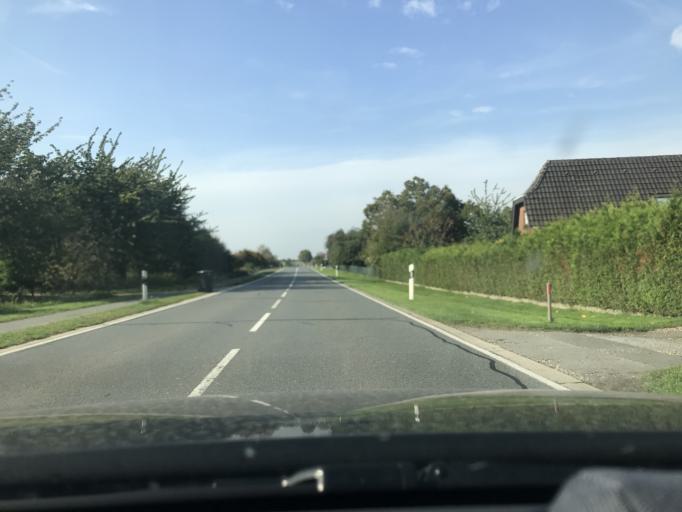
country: DE
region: North Rhine-Westphalia
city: Kalkar
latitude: 51.7337
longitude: 6.2633
